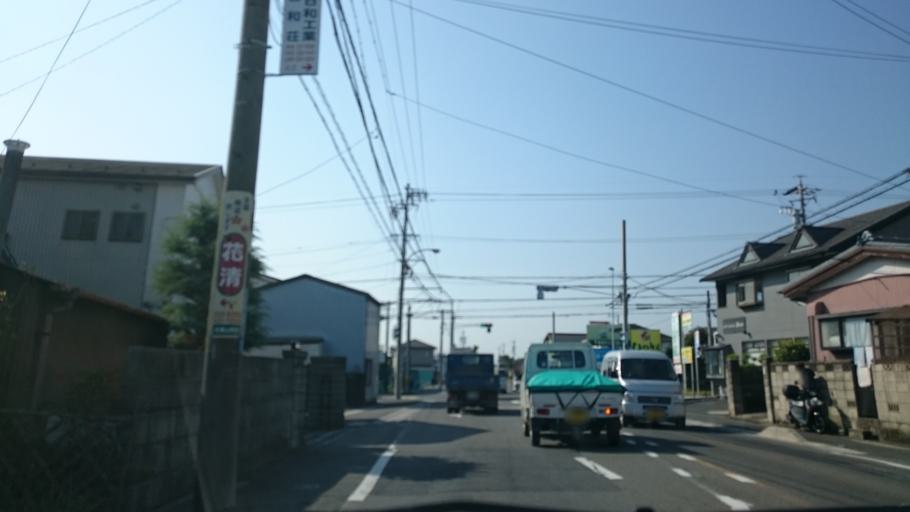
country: JP
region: Mie
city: Yokkaichi
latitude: 34.9911
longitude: 136.6244
